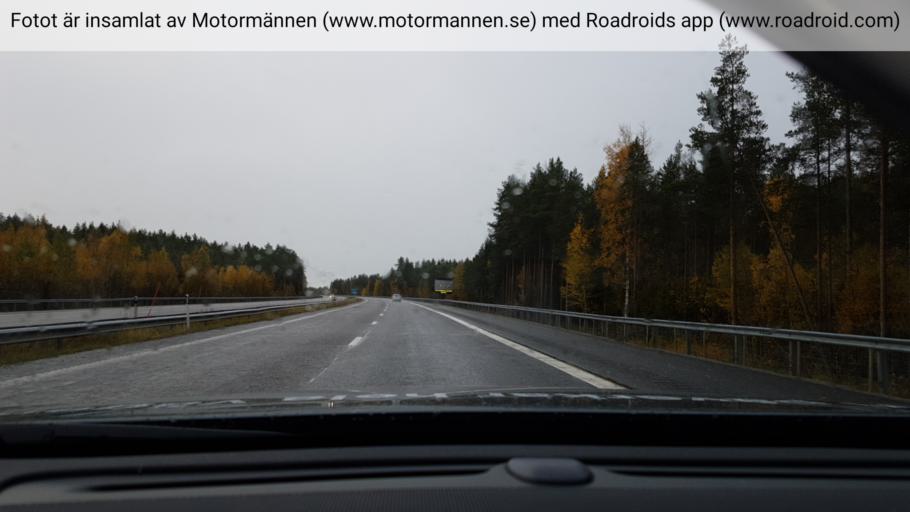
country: SE
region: Norrbotten
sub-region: Pitea Kommun
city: Pitea
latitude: 65.3454
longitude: 21.4373
